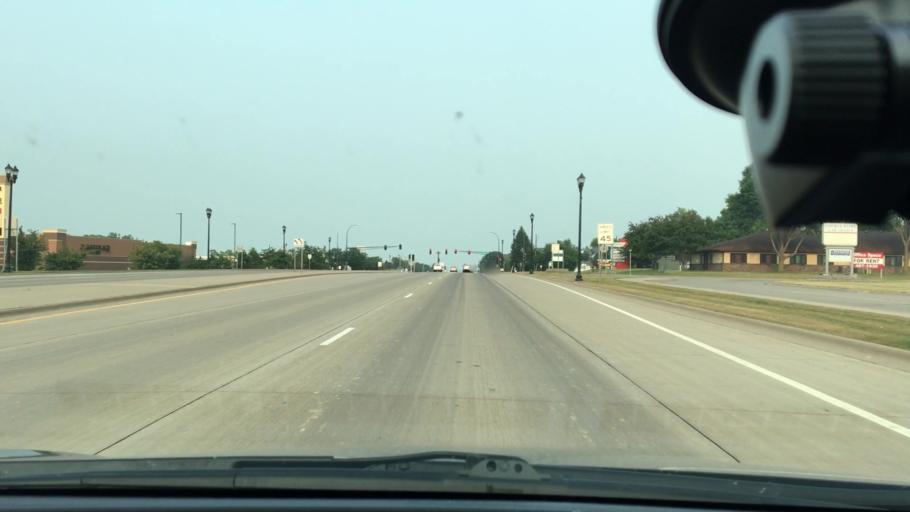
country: US
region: Minnesota
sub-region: Wright County
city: Saint Michael
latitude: 45.2100
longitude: -93.6503
